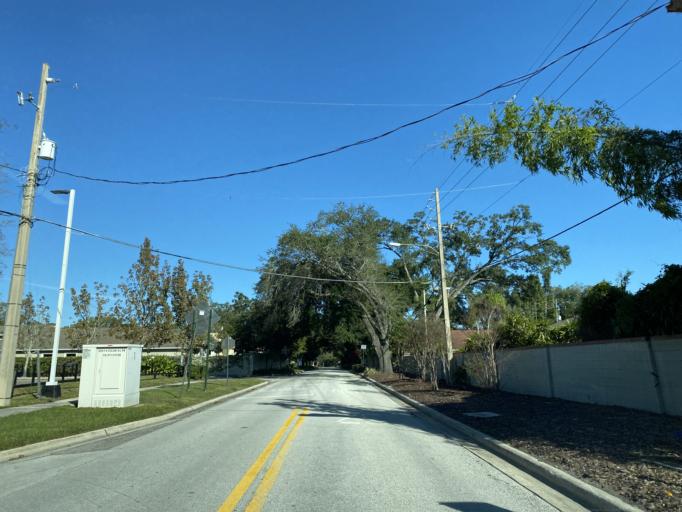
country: US
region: Florida
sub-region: Orange County
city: Orlando
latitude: 28.5534
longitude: -81.4057
